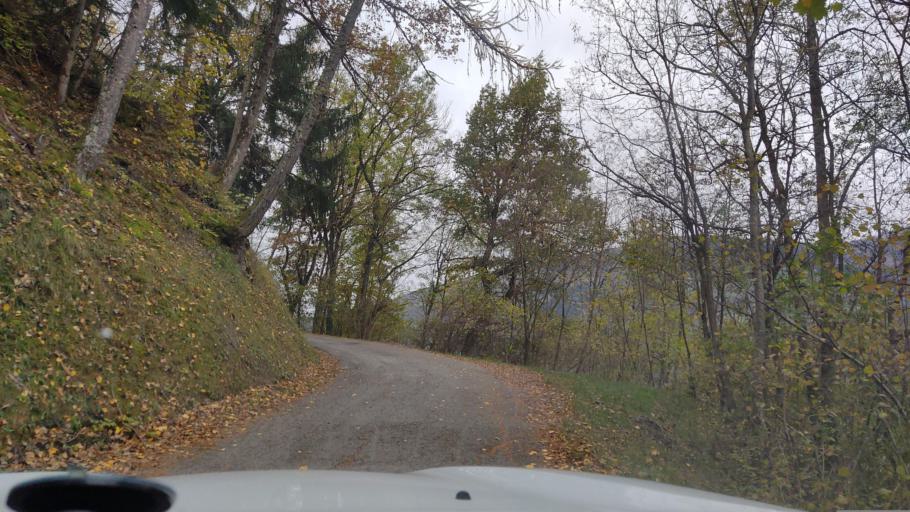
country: FR
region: Rhone-Alpes
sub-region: Departement de la Savoie
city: Bourg-Saint-Maurice
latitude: 45.6092
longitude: 6.7770
